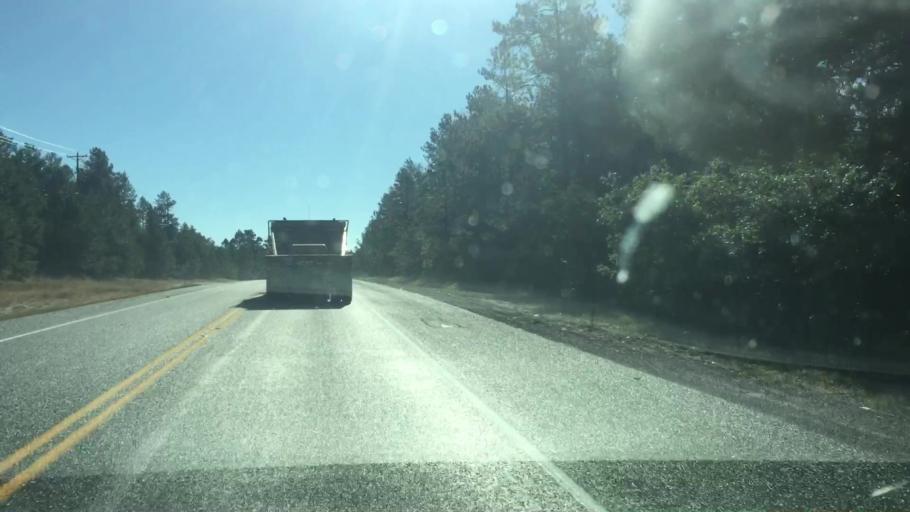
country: US
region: Colorado
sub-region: Douglas County
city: The Pinery
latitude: 39.3849
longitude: -104.7300
